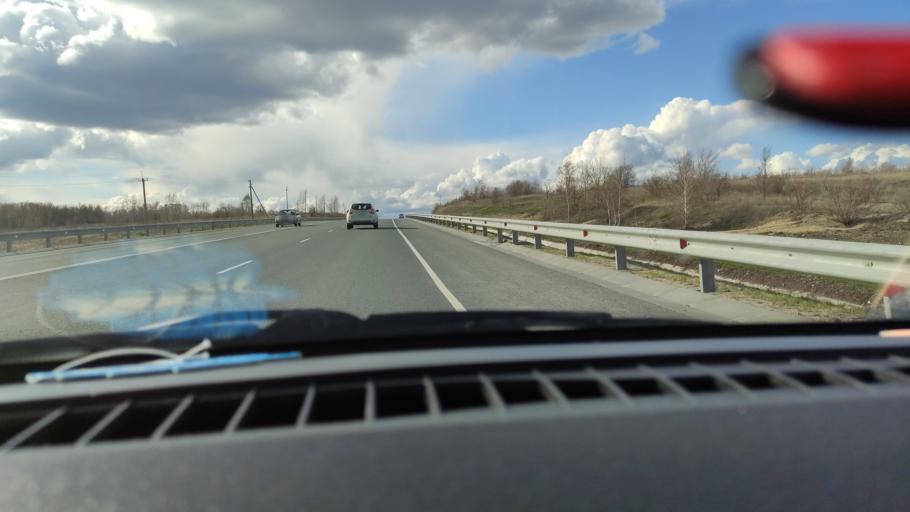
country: RU
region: Saratov
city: Shikhany
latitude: 52.1428
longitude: 47.2037
